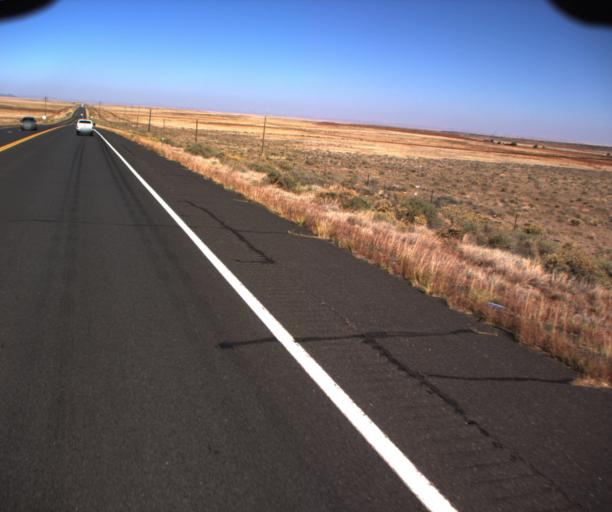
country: US
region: Arizona
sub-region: Coconino County
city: Flagstaff
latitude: 35.6562
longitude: -111.5143
